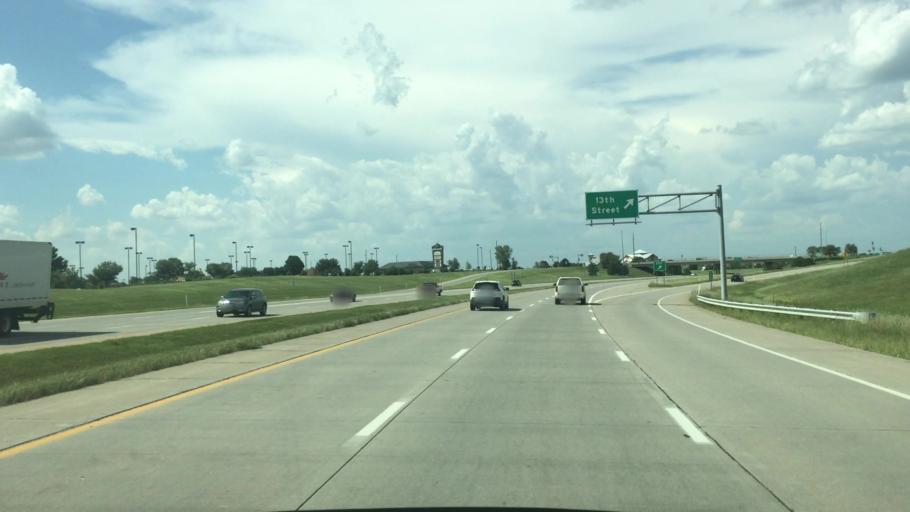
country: US
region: Kansas
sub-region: Butler County
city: Andover
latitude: 37.7043
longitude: -97.1996
